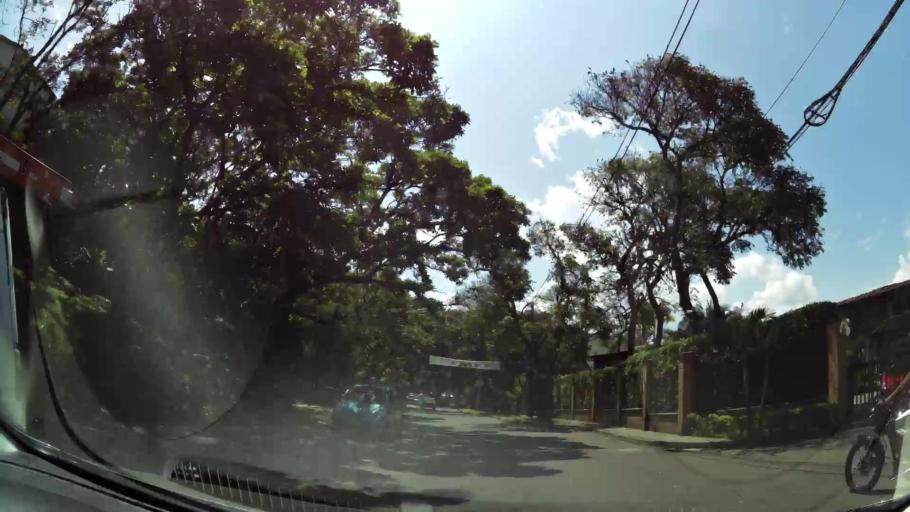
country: CO
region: Antioquia
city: Itagui
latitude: 6.2109
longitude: -75.5990
